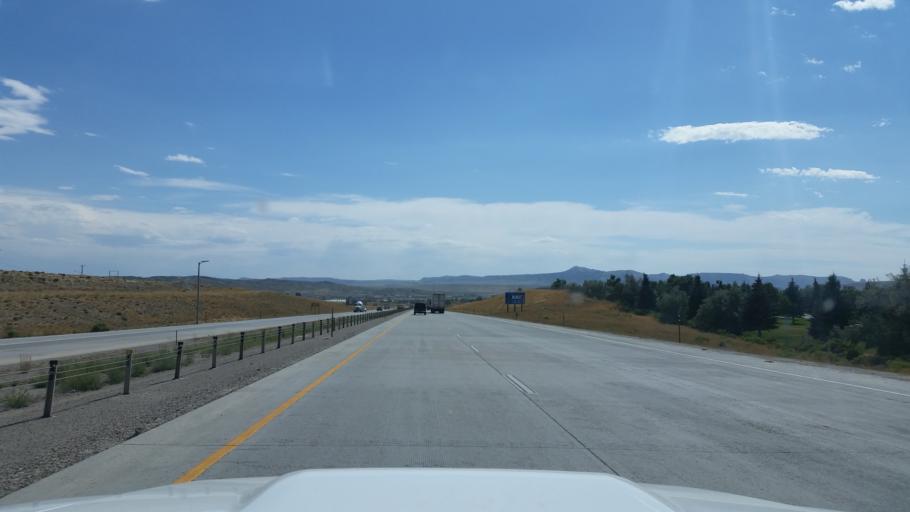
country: US
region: Wyoming
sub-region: Sweetwater County
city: Rock Springs
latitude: 41.5944
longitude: -109.2441
